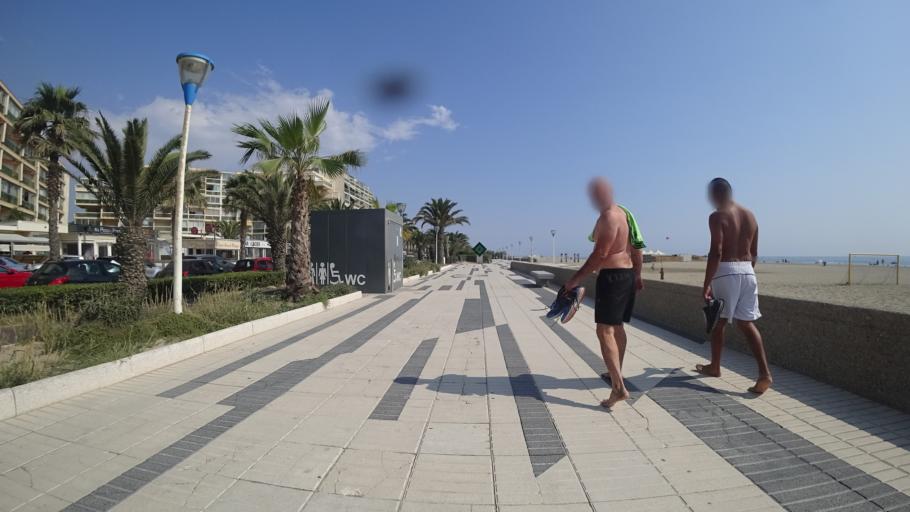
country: FR
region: Languedoc-Roussillon
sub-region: Departement des Pyrenees-Orientales
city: Canet-en-Roussillon
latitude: 42.6805
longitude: 3.0343
